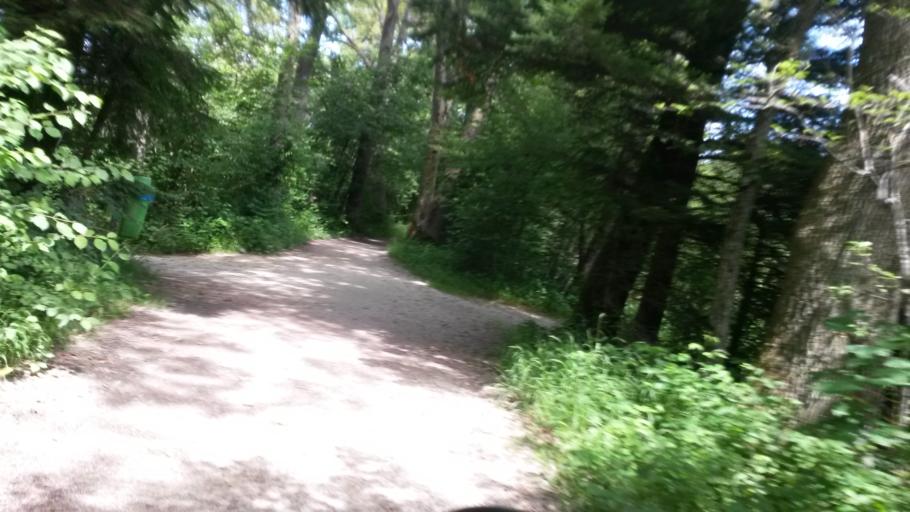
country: DE
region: Bavaria
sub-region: Upper Bavaria
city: Ubersee
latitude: 47.8598
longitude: 12.4771
